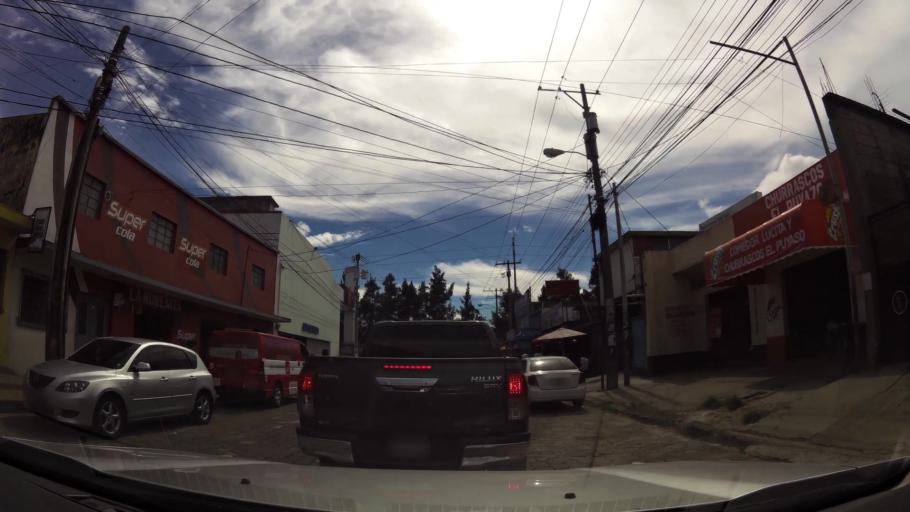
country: GT
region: Guatemala
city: Mixco
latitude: 14.6347
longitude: -90.5784
